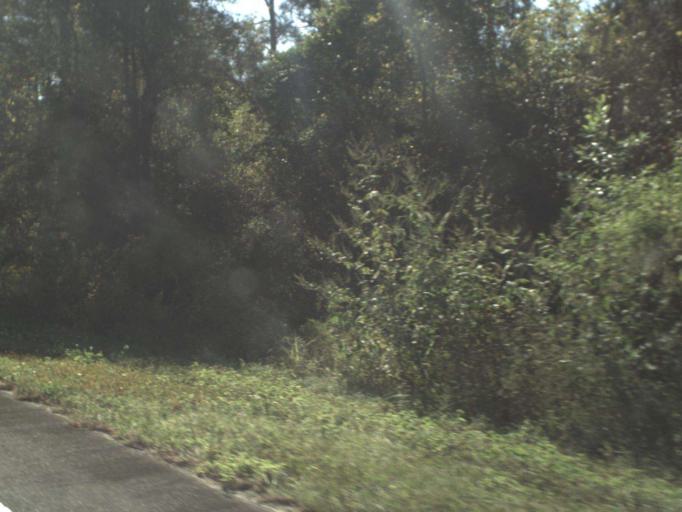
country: US
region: Florida
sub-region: Gadsden County
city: Midway
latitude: 30.3453
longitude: -84.5017
